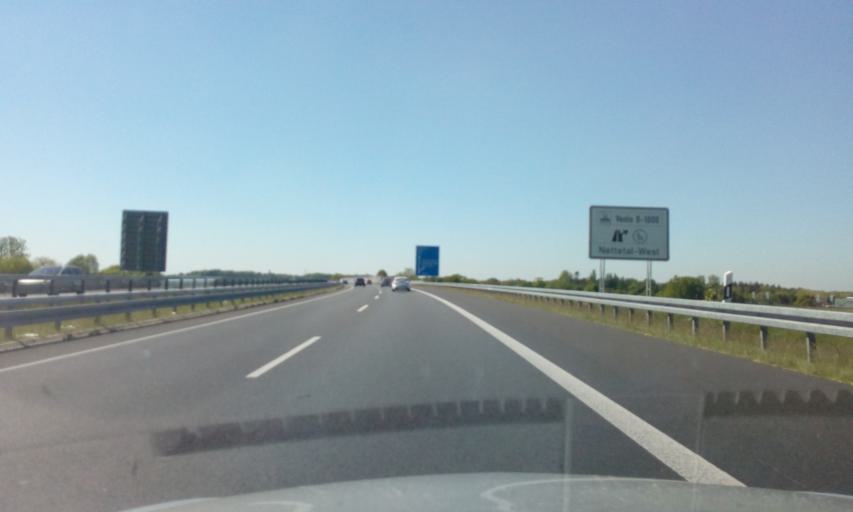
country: NL
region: Limburg
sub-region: Gemeente Venlo
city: Venlo
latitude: 51.3341
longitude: 6.2014
